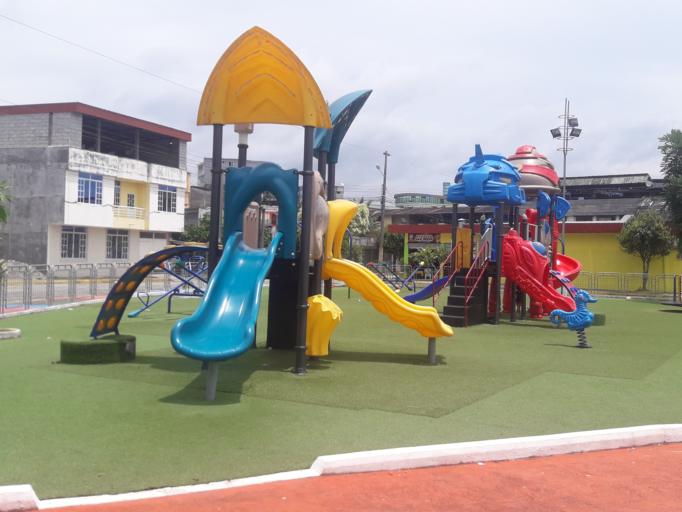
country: EC
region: Napo
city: Tena
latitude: -0.9937
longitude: -77.8120
